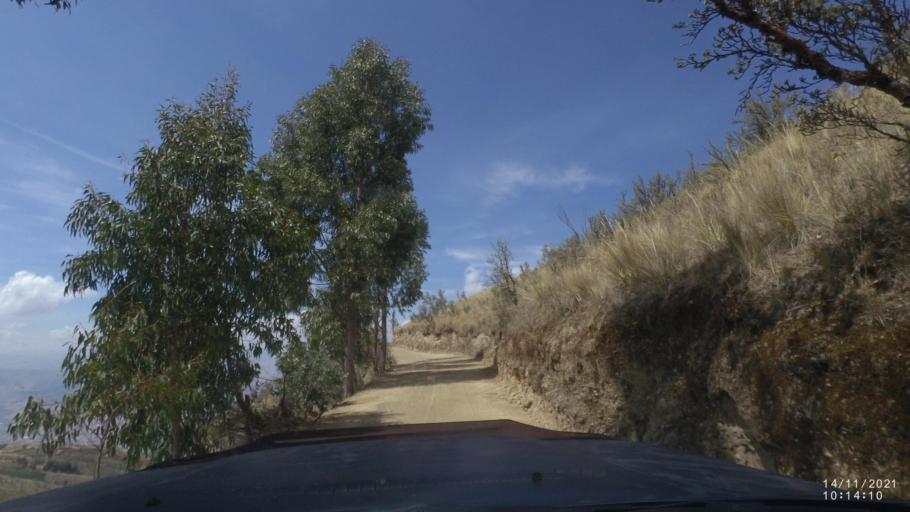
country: BO
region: Cochabamba
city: Cochabamba
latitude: -17.3430
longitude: -66.0874
